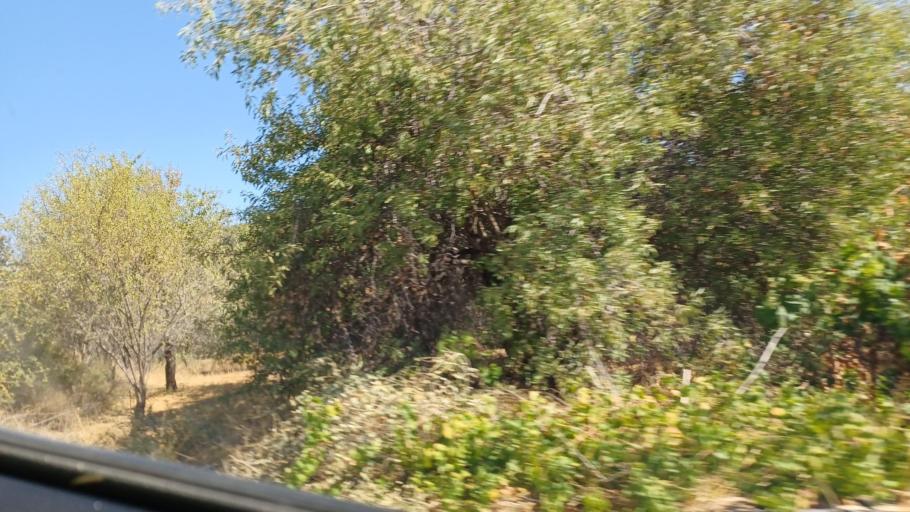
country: CY
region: Pafos
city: Mesogi
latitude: 34.9233
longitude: 32.5709
